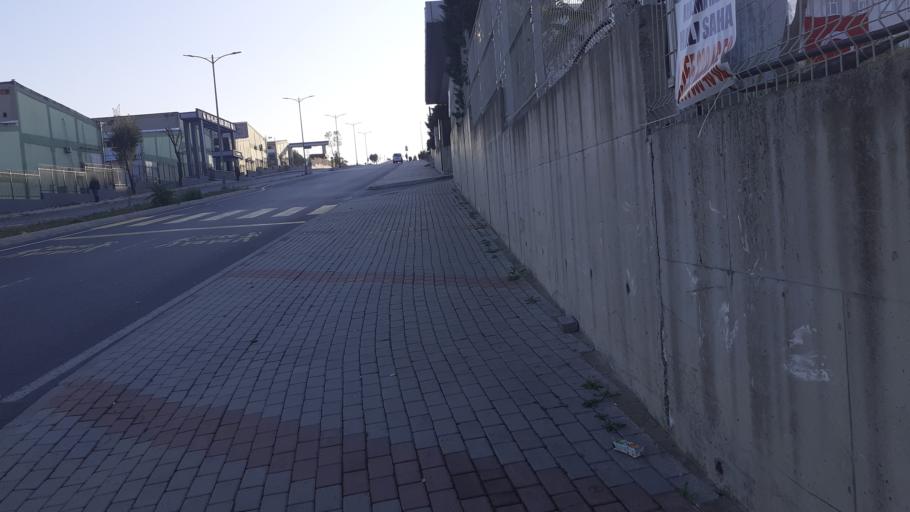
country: TR
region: Istanbul
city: Basaksehir
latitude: 41.0691
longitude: 28.7831
